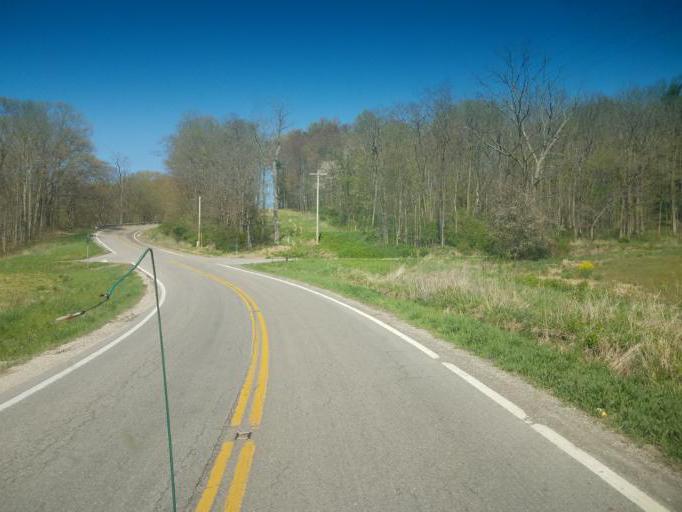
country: US
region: Ohio
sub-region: Medina County
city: Lodi
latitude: 40.9391
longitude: -82.0131
